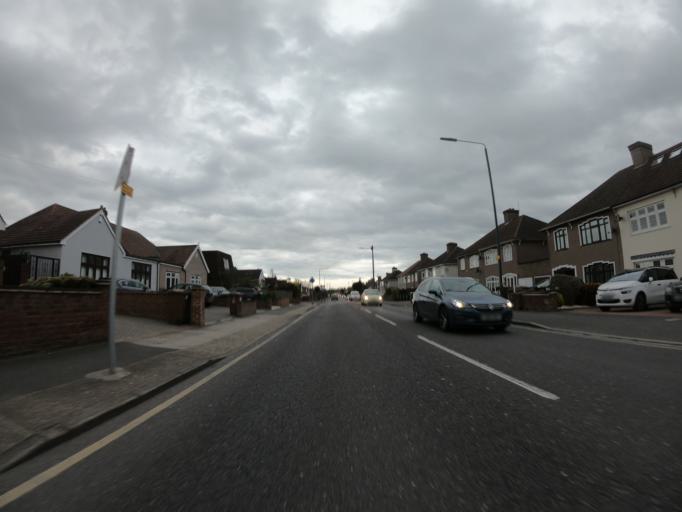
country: GB
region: England
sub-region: Greater London
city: Bexleyheath
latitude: 51.4687
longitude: 0.1299
